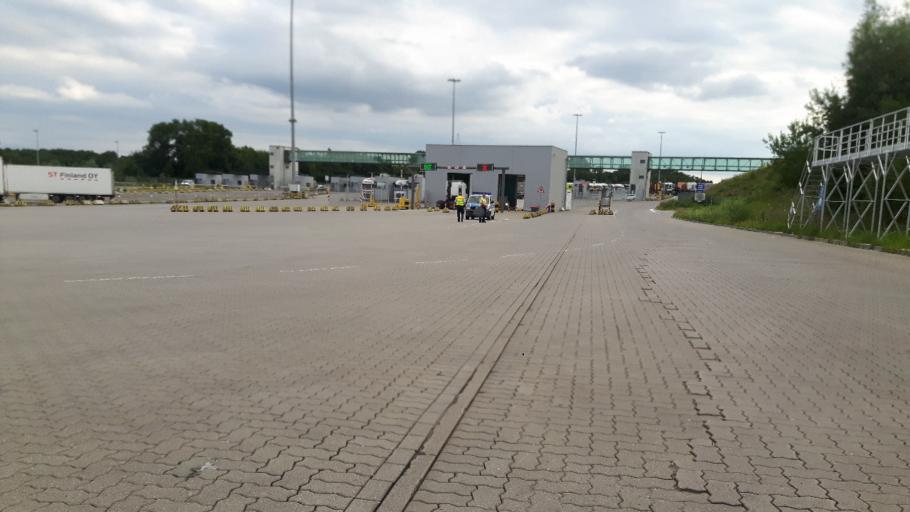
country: DE
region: Schleswig-Holstein
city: Travemuende
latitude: 53.9412
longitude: 10.8556
